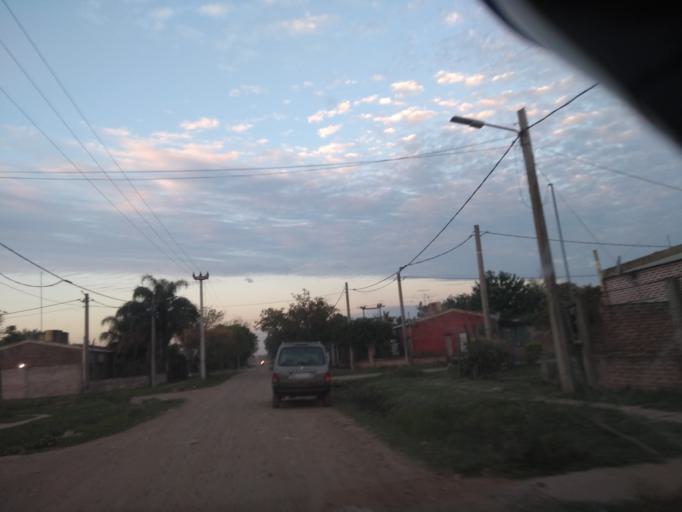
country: AR
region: Chaco
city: Fontana
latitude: -27.4066
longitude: -59.0478
